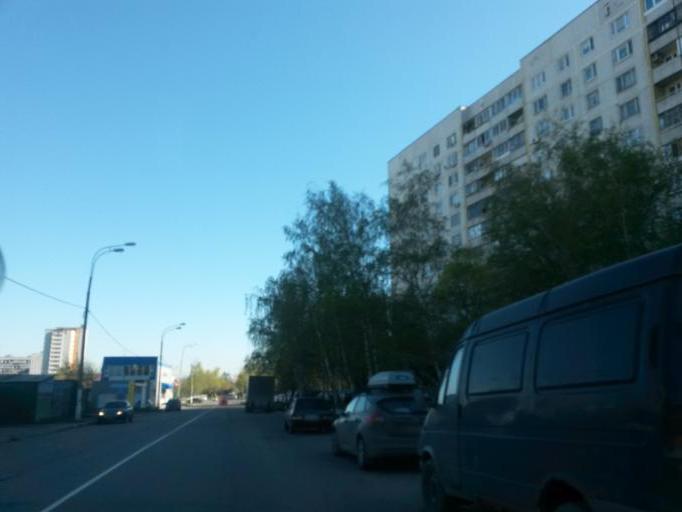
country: RU
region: Moscow
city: Orekhovo-Borisovo
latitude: 55.6201
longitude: 37.7299
